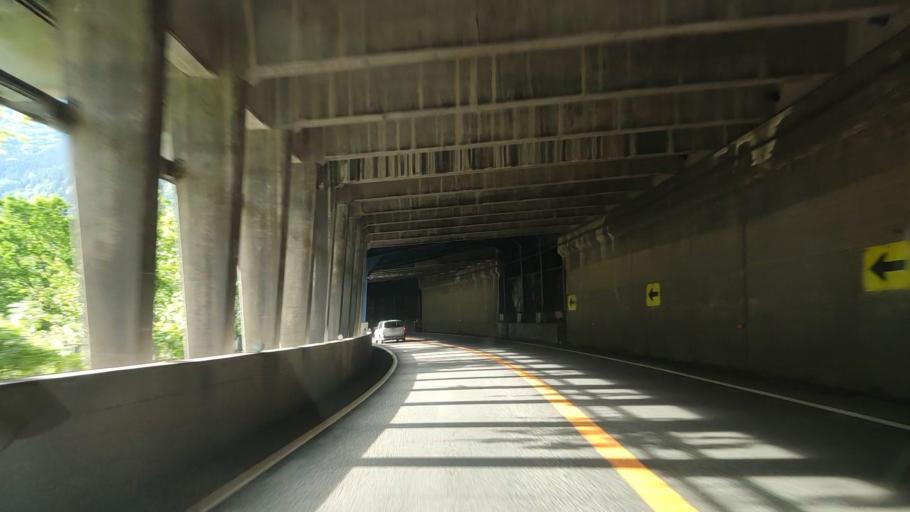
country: JP
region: Toyama
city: Yatsuomachi-higashikumisaka
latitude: 36.4462
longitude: 137.2733
